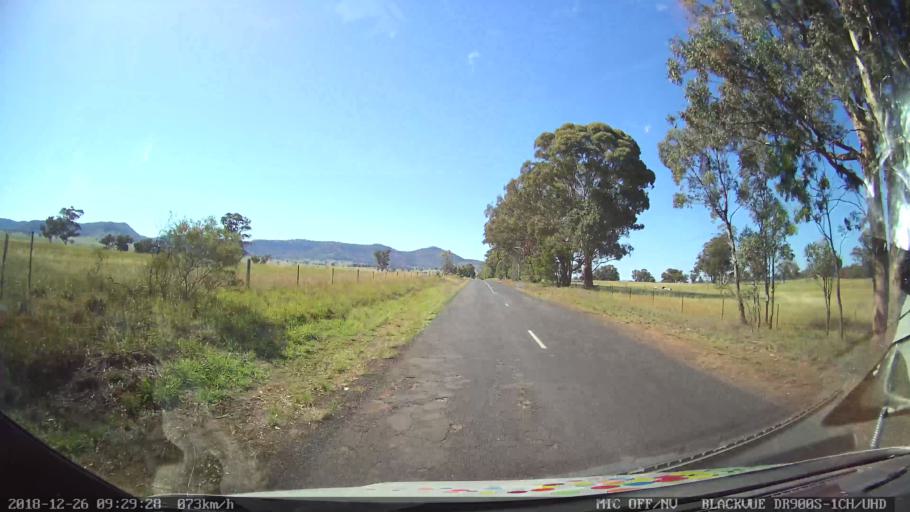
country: AU
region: New South Wales
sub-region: Mid-Western Regional
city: Kandos
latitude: -32.8532
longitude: 150.0276
